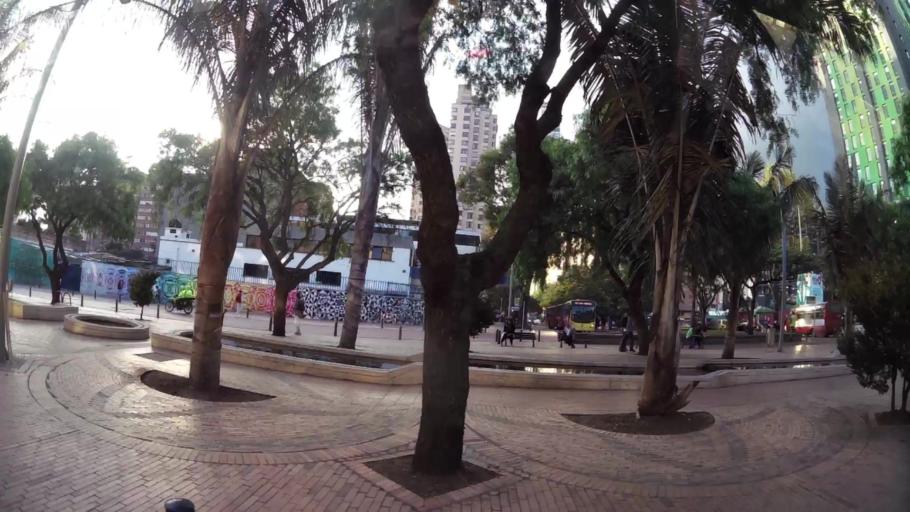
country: CO
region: Bogota D.C.
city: Bogota
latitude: 4.6023
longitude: -74.0674
